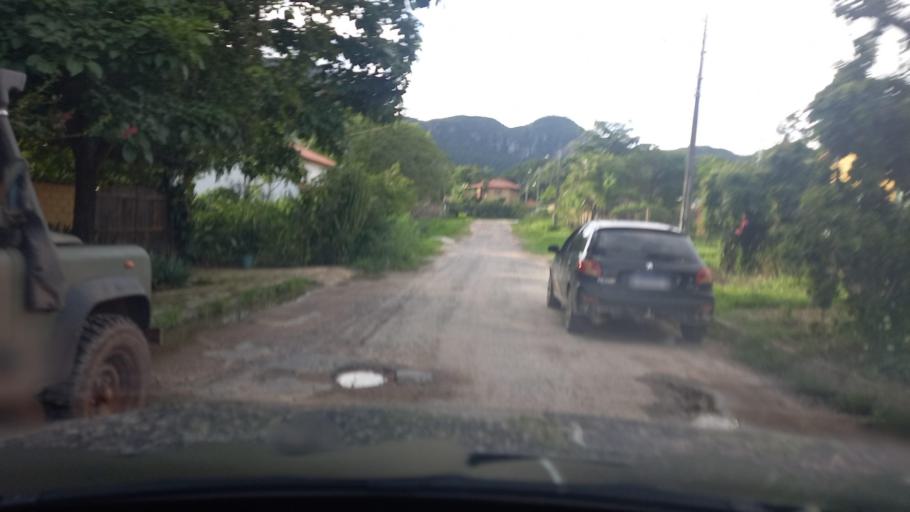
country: BR
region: Goias
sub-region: Cavalcante
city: Cavalcante
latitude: -13.7930
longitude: -47.4631
